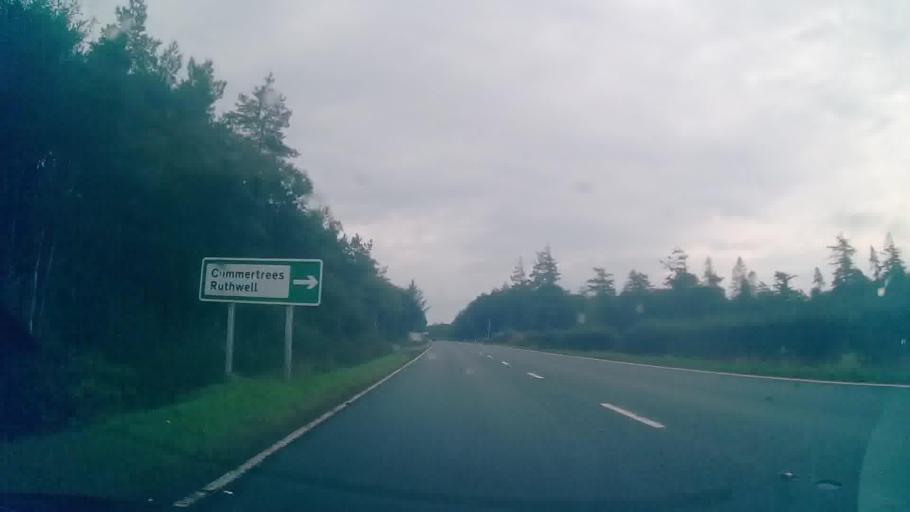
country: GB
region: Scotland
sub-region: Dumfries and Galloway
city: Annan
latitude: 55.0138
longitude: -3.3528
